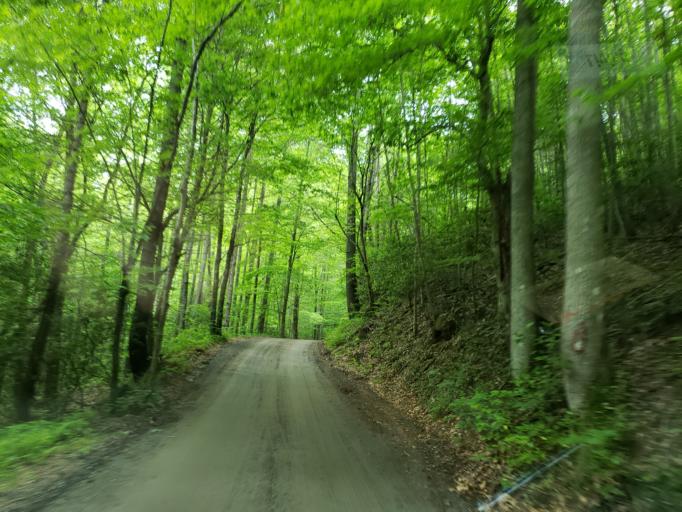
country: US
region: Georgia
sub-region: Fannin County
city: Blue Ridge
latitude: 34.8548
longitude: -84.4333
